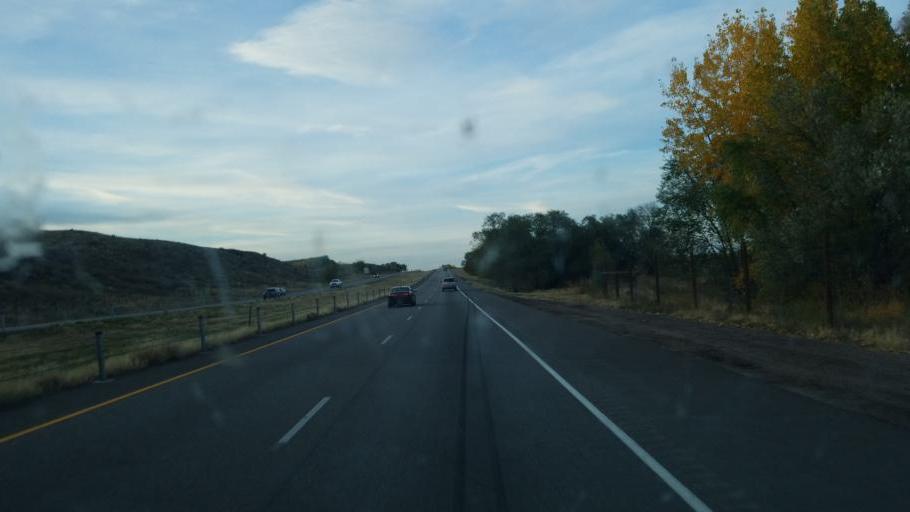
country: US
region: Colorado
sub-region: El Paso County
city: Fountain
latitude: 38.6377
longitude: -104.6925
